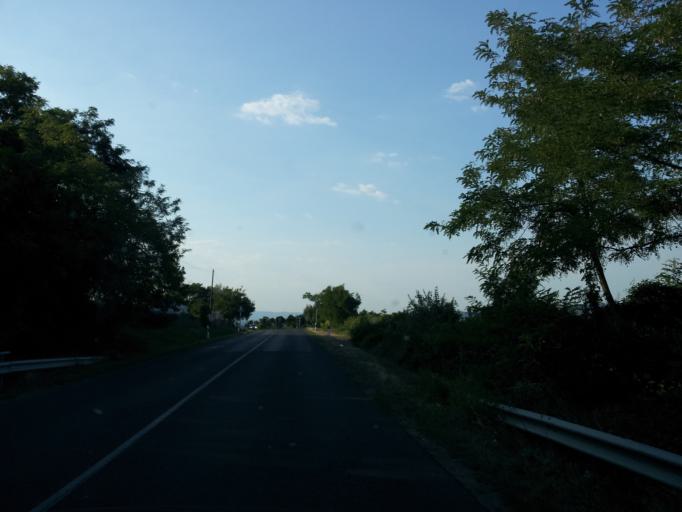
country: HU
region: Pest
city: Dunabogdany
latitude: 47.7707
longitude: 19.0595
